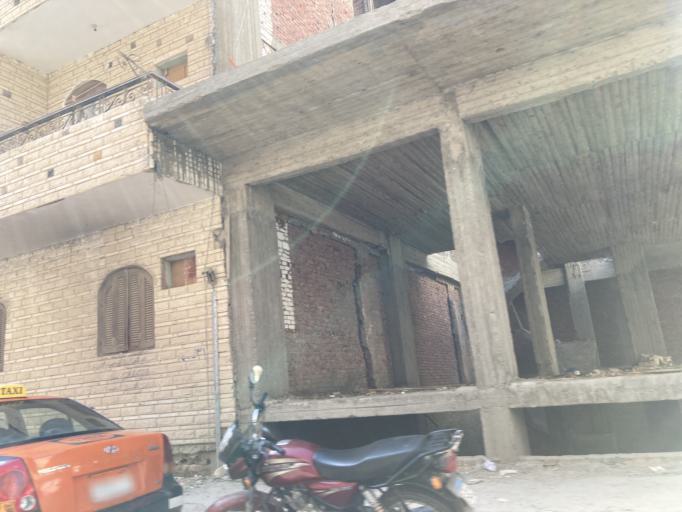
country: EG
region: Red Sea
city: Hurghada
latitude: 27.2498
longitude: 33.8327
